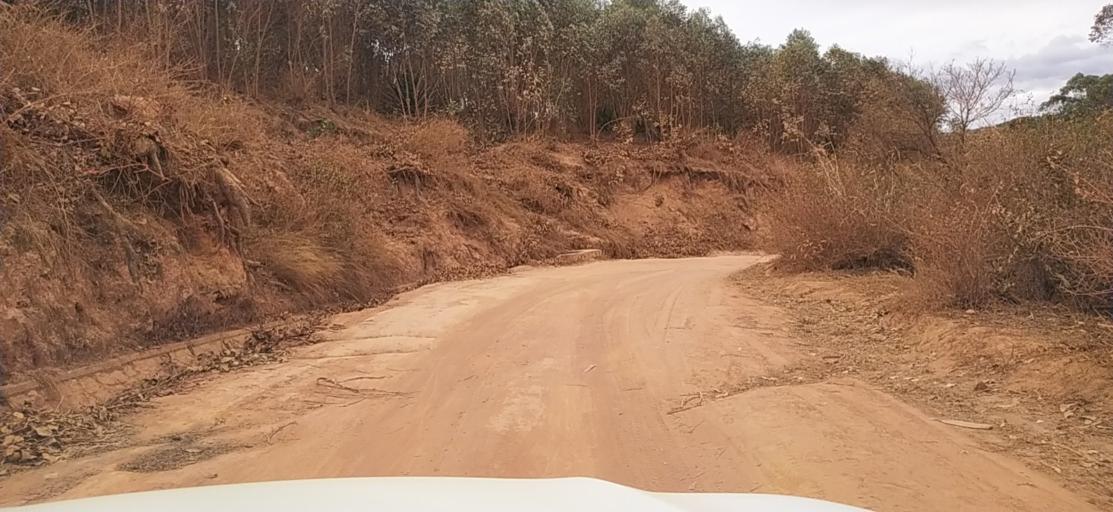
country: MG
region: Alaotra Mangoro
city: Ambatondrazaka
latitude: -18.0057
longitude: 48.2605
